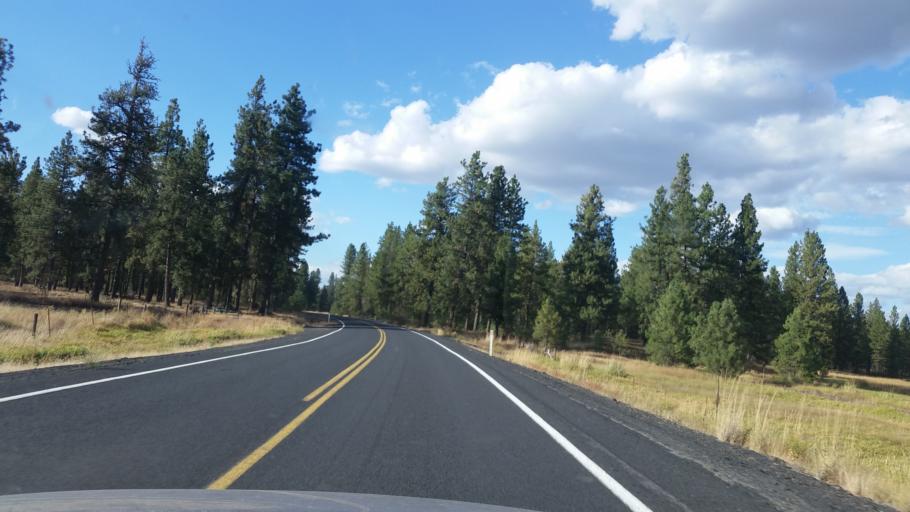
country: US
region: Washington
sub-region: Spokane County
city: Cheney
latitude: 47.4262
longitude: -117.5653
